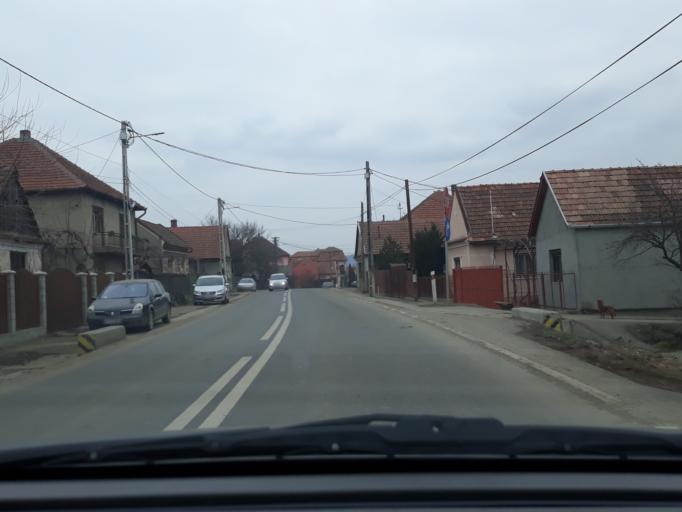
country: RO
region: Salaj
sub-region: Comuna Nusfalau
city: Nusfalau
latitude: 47.1930
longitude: 22.7012
